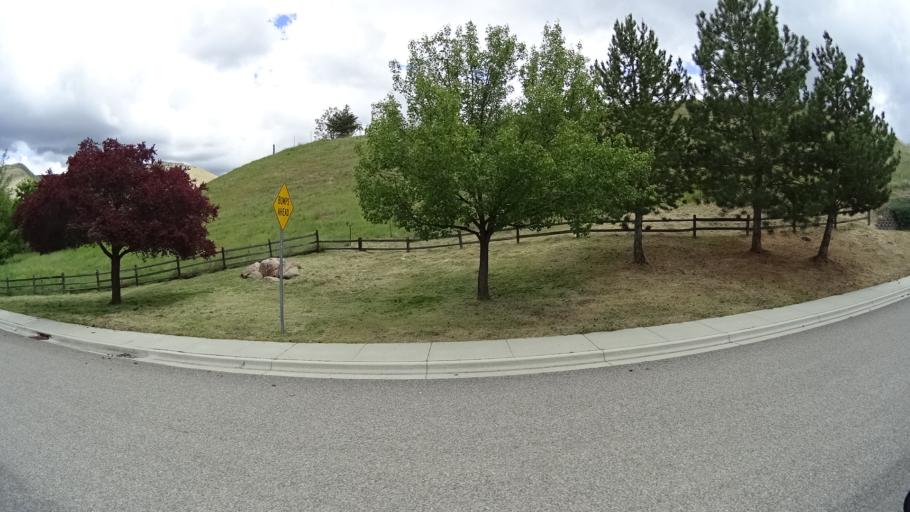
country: US
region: Idaho
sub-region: Ada County
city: Garden City
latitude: 43.6660
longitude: -116.2135
